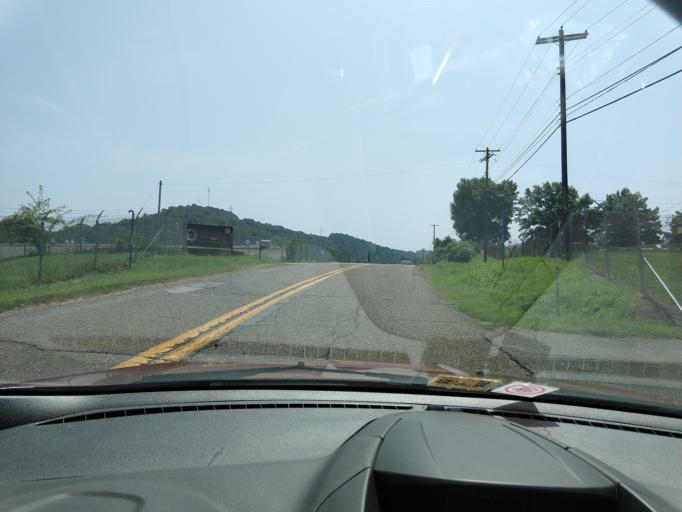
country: US
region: West Virginia
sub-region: Harrison County
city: Clarksburg
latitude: 39.2691
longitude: -80.3673
